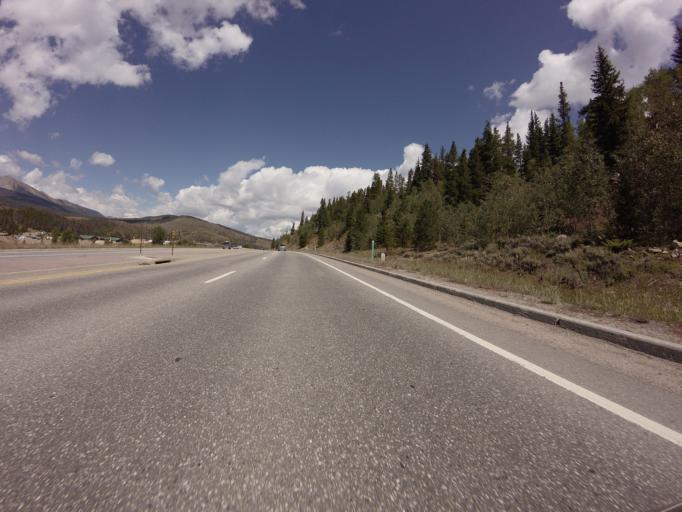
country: US
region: Colorado
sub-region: Summit County
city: Breckenridge
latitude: 39.5085
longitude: -106.0480
